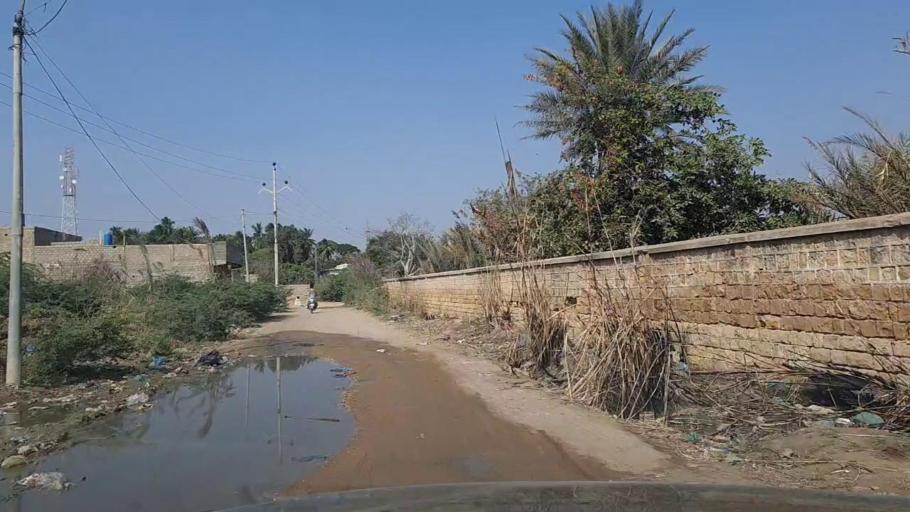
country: PK
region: Sindh
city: Gharo
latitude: 24.7448
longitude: 67.5824
